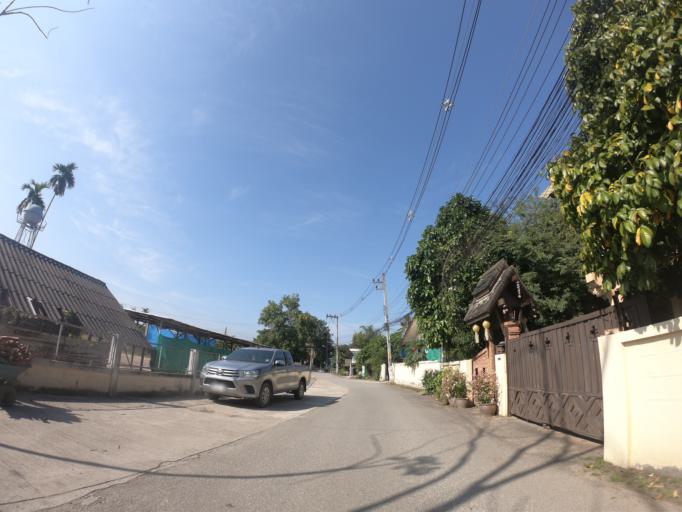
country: TH
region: Chiang Mai
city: Saraphi
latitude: 18.7679
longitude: 99.0448
